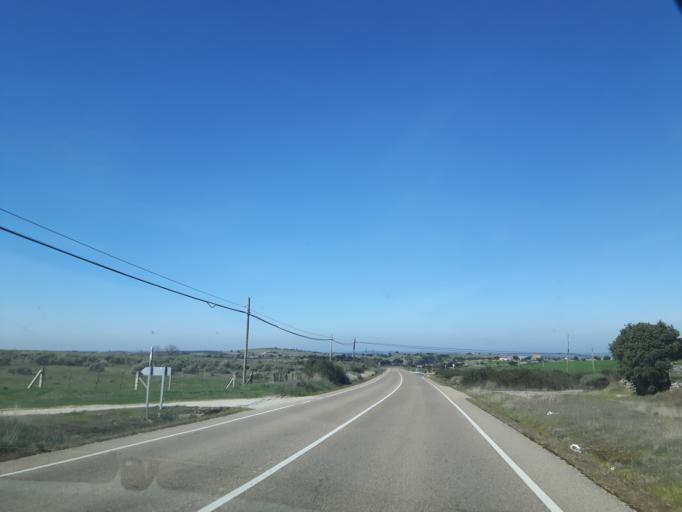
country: ES
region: Castille and Leon
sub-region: Provincia de Salamanca
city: Guadramiro
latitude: 41.0122
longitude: -6.4783
